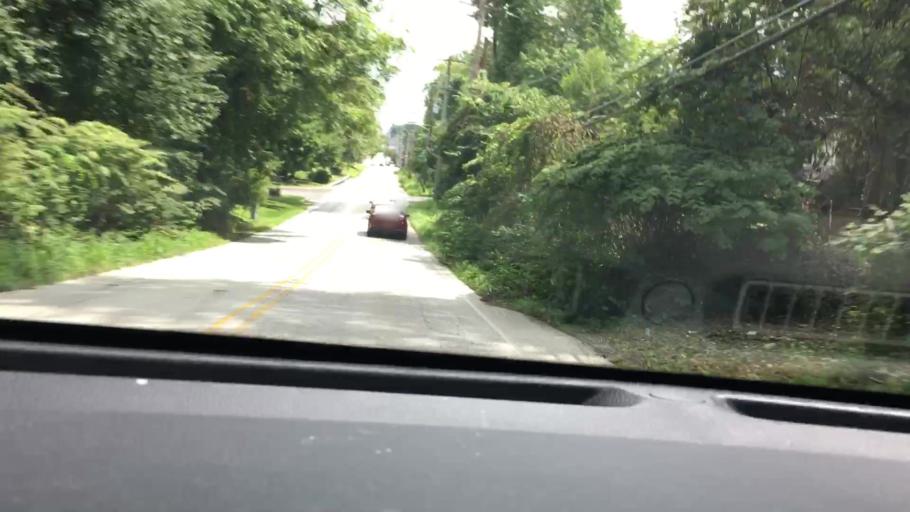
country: US
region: Pennsylvania
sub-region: Bucks County
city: Feasterville
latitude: 40.1309
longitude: -75.0278
